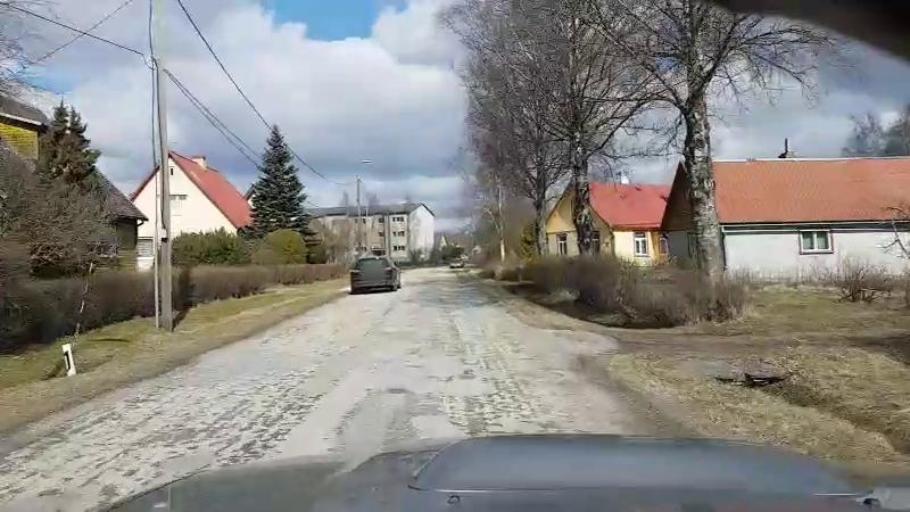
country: EE
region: Jaervamaa
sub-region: Paide linn
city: Paide
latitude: 58.8833
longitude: 25.5778
